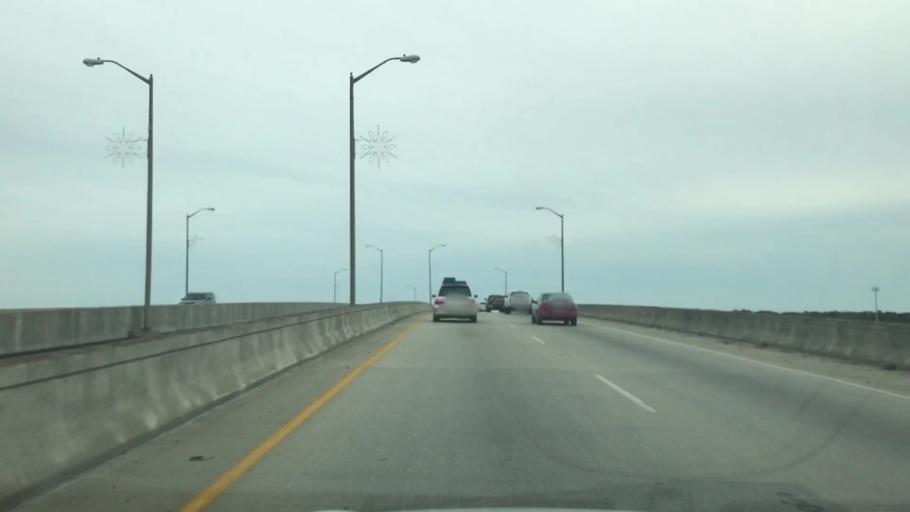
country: US
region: South Carolina
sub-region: Georgetown County
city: Georgetown
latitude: 33.3594
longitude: -79.2948
